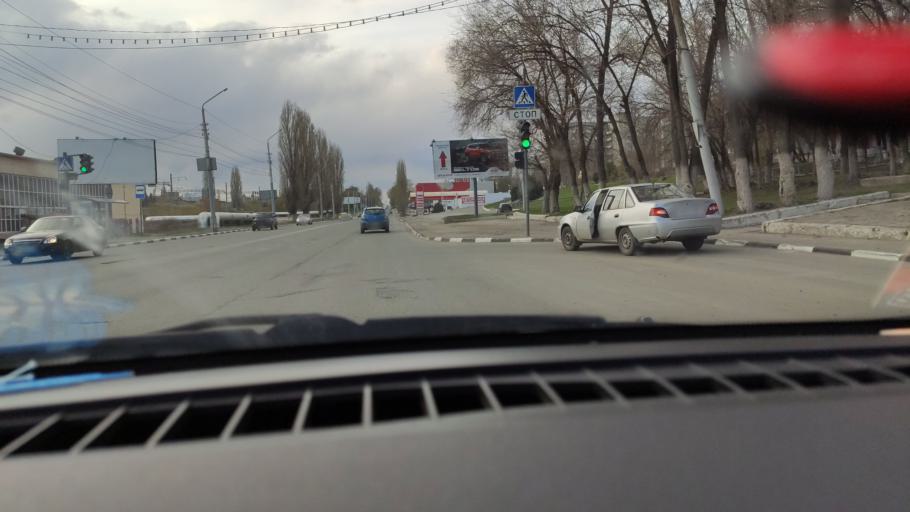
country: RU
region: Saratov
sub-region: Saratovskiy Rayon
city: Saratov
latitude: 51.5707
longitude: 45.9947
